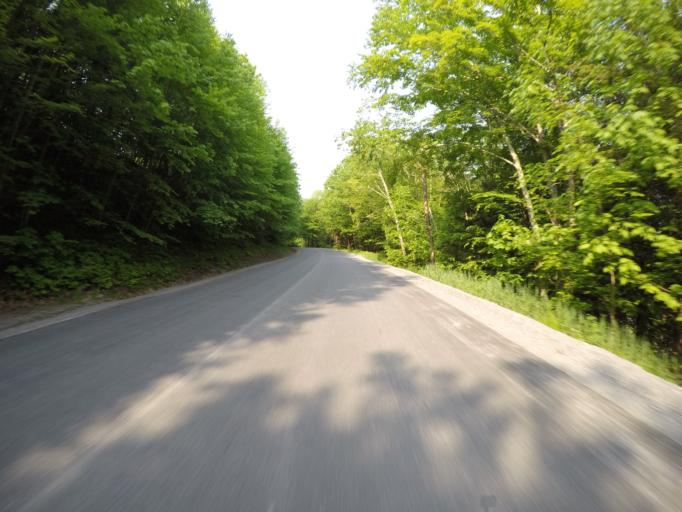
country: US
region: New York
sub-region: Sullivan County
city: Livingston Manor
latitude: 42.1231
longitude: -74.6980
